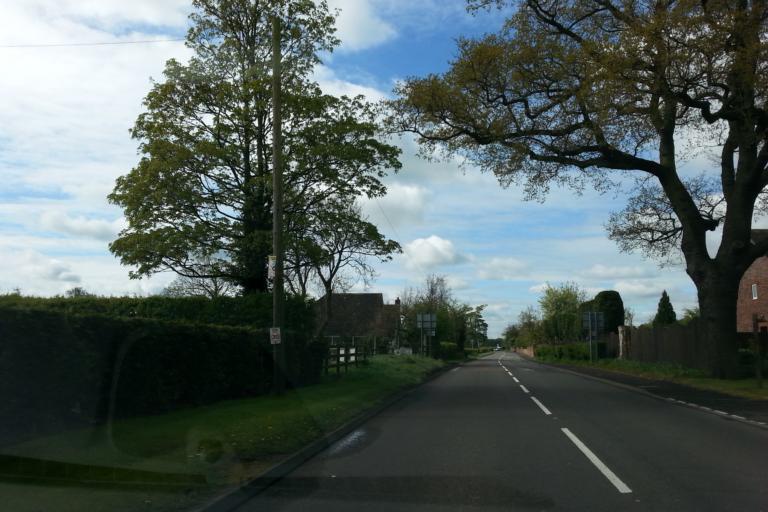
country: GB
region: England
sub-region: Staffordshire
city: Armitage
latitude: 52.7464
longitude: -1.8238
